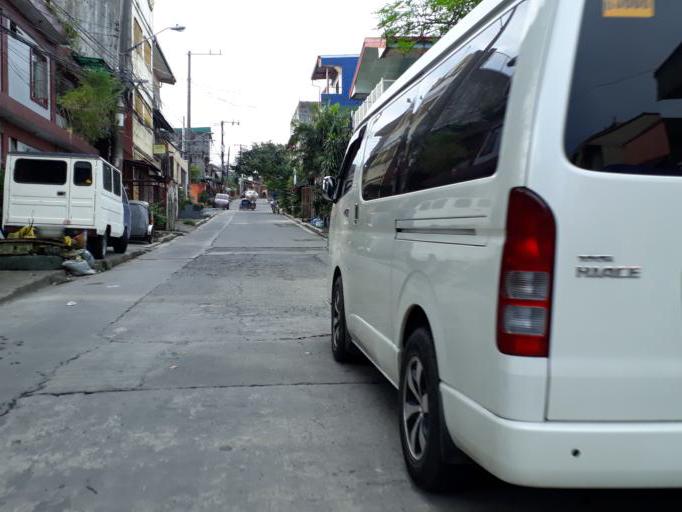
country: PH
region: Calabarzon
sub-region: Province of Rizal
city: Valenzuela
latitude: 14.6772
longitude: 120.9879
